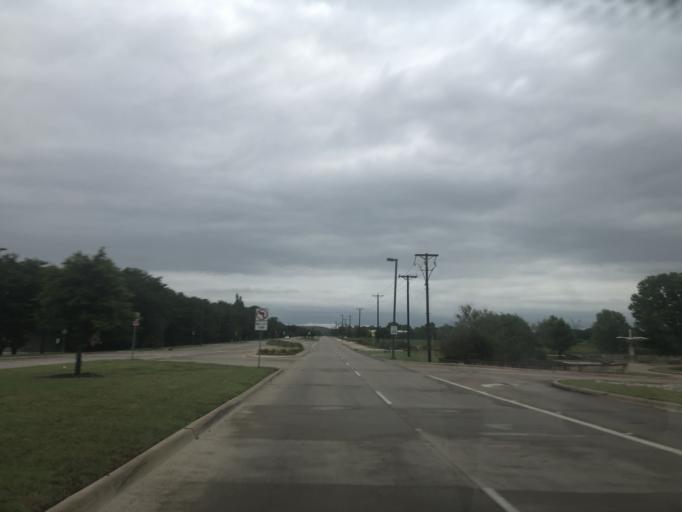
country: US
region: Texas
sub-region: Dallas County
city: Irving
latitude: 32.7829
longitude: -96.9738
